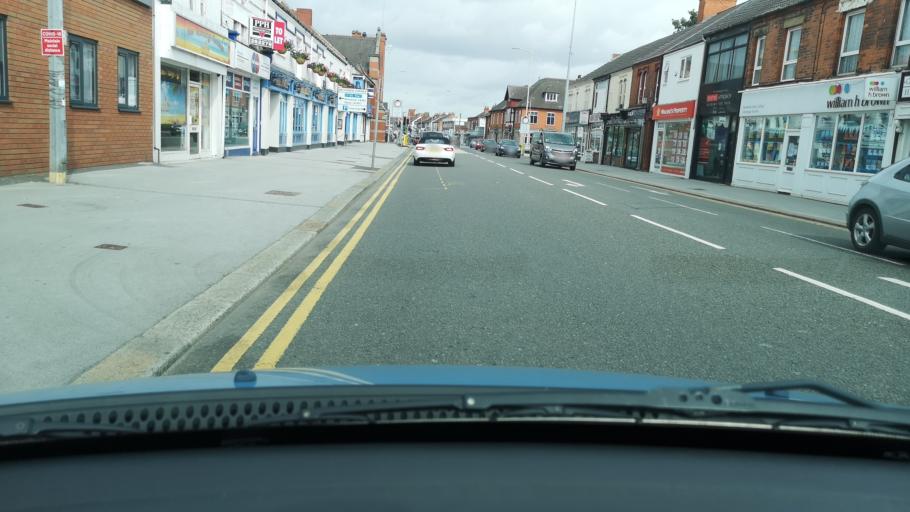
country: GB
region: England
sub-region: North Lincolnshire
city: Scunthorpe
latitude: 53.5900
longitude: -0.6541
